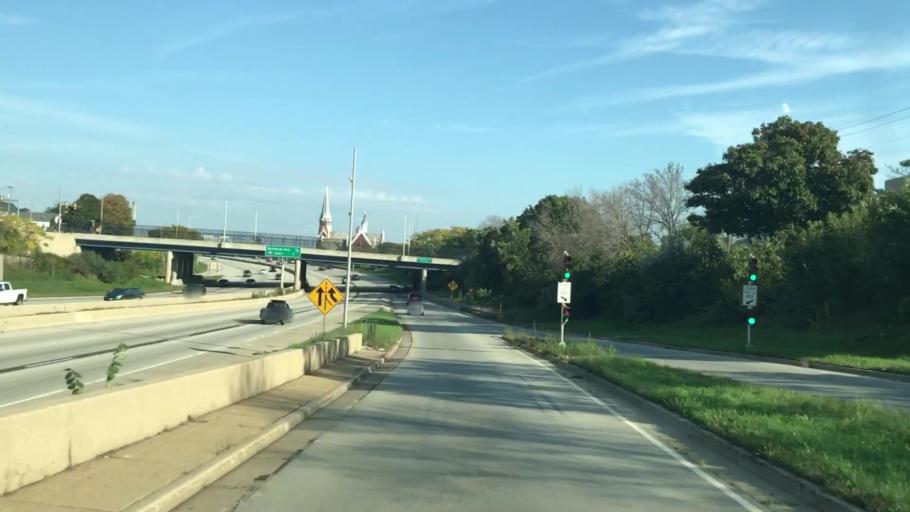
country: US
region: Wisconsin
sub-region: Milwaukee County
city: Milwaukee
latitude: 43.0156
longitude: -87.9158
